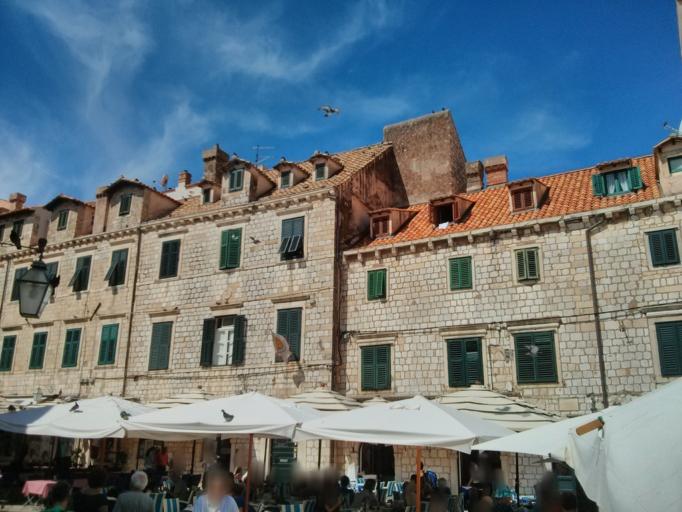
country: HR
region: Dubrovacko-Neretvanska
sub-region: Grad Dubrovnik
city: Dubrovnik
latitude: 42.6402
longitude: 18.1100
